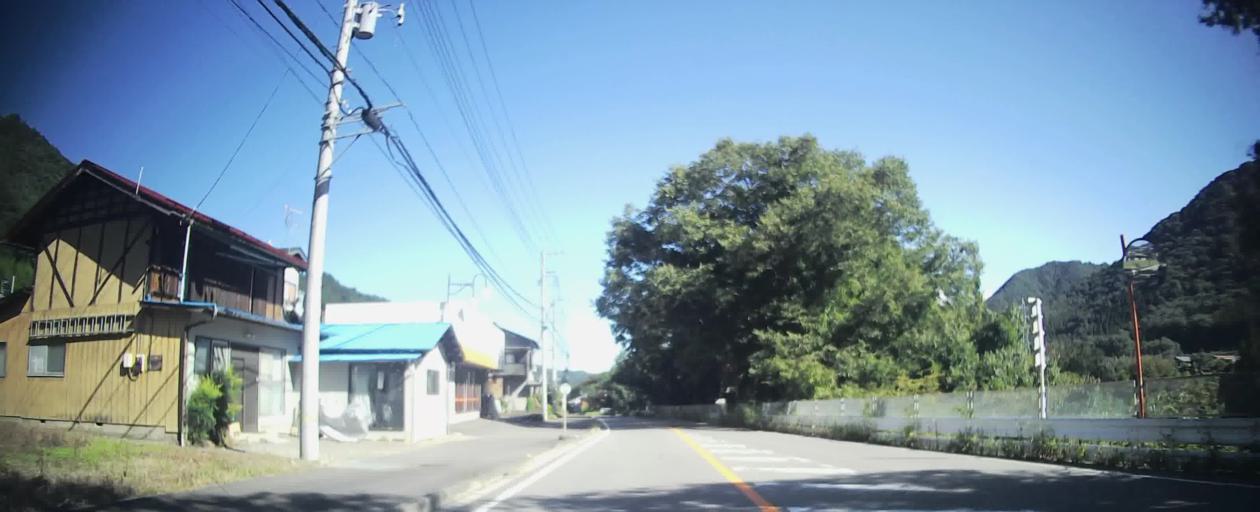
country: JP
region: Gunma
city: Nakanojomachi
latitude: 36.5727
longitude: 138.7360
